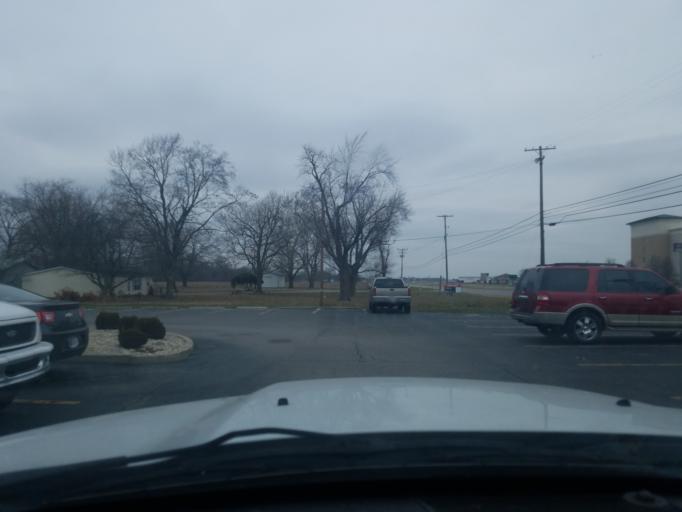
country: US
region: Indiana
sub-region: Johnson County
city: Edinburgh
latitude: 39.3117
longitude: -85.9663
